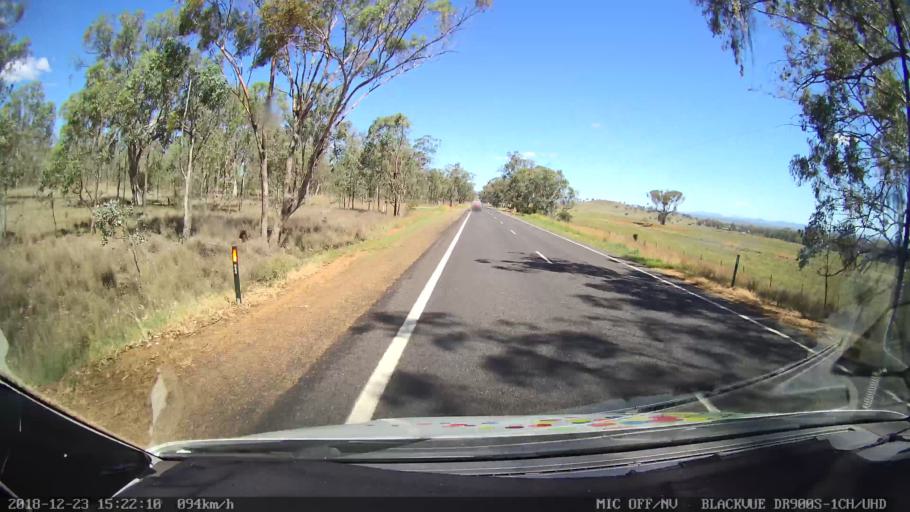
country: AU
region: New South Wales
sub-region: Tamworth Municipality
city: Manilla
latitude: -30.8650
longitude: 150.8024
